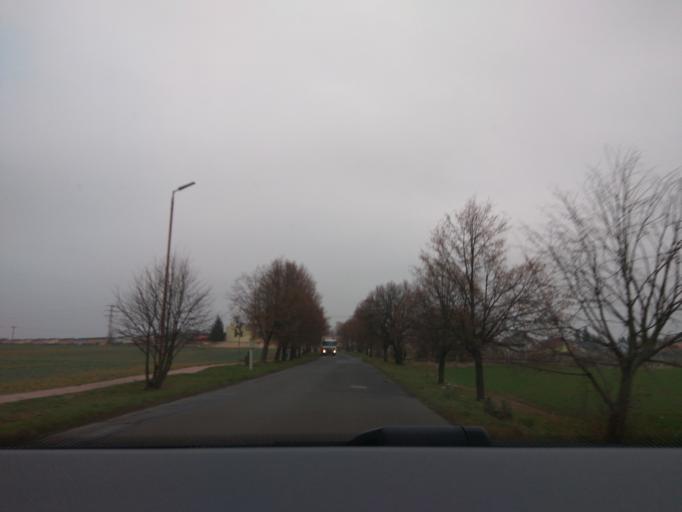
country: CZ
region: Central Bohemia
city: Hovorcovice
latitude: 50.1702
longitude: 14.5463
